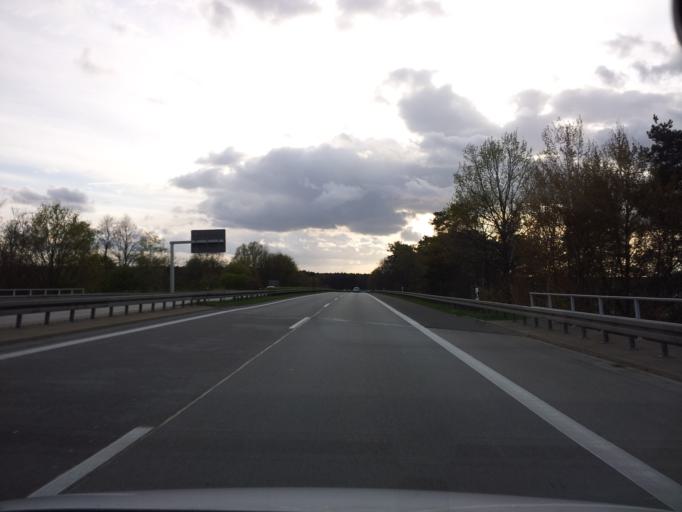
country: DE
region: Brandenburg
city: Kolkwitz
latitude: 51.7240
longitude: 14.2813
